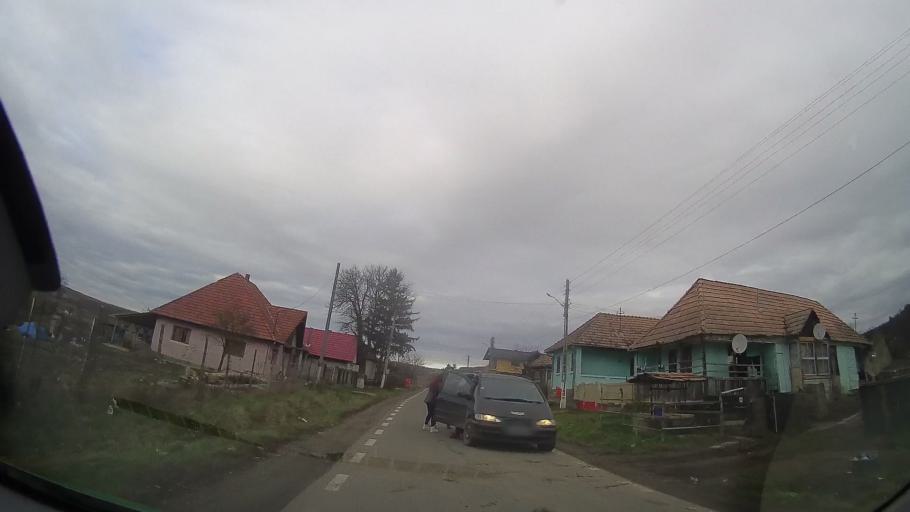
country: RO
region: Mures
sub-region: Comuna Faragau
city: Faragau
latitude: 46.7820
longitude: 24.5510
